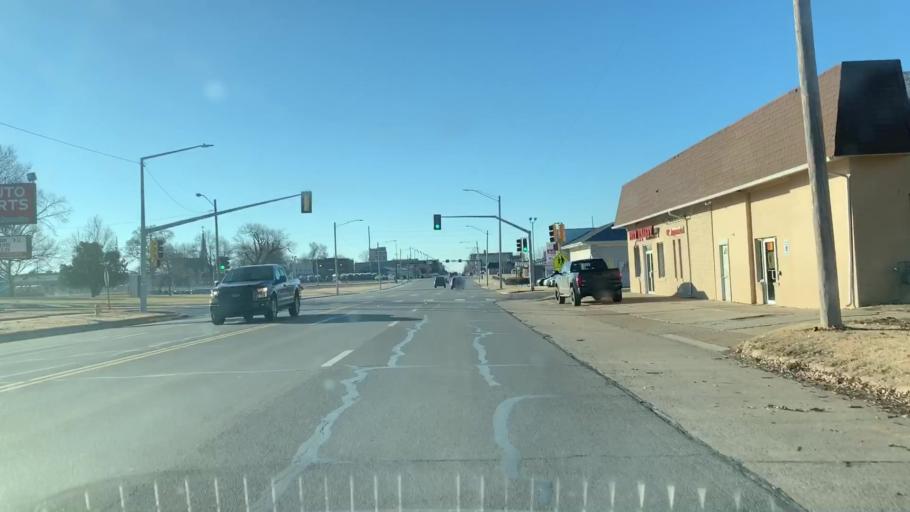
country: US
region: Kansas
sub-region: Crawford County
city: Pittsburg
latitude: 37.4207
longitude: -94.7050
